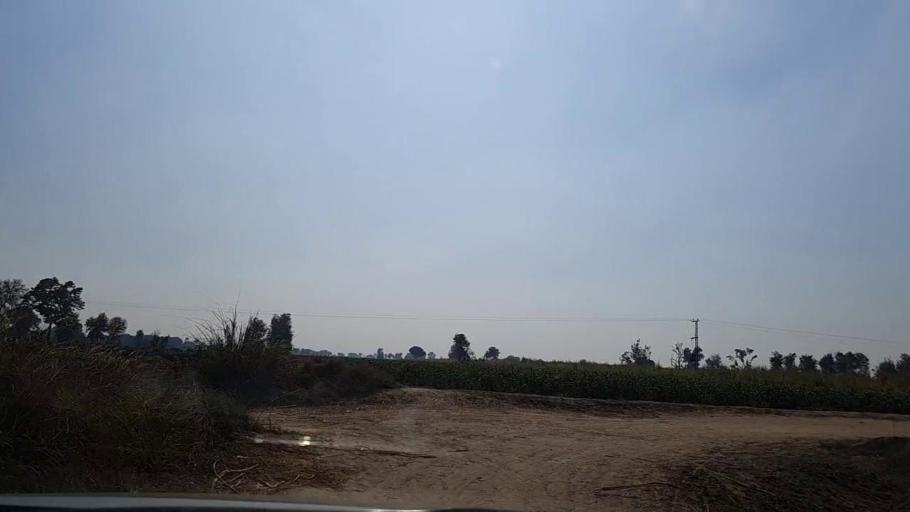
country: PK
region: Sindh
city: Daulatpur
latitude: 26.2891
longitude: 68.0648
